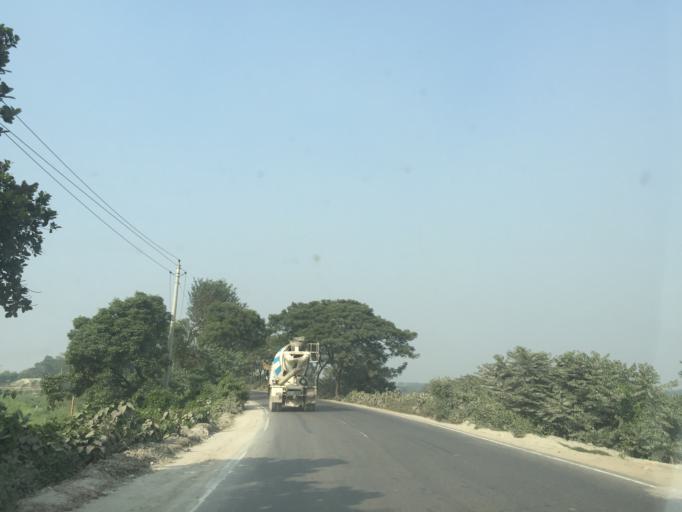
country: BD
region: Dhaka
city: Tungi
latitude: 23.8420
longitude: 90.3431
